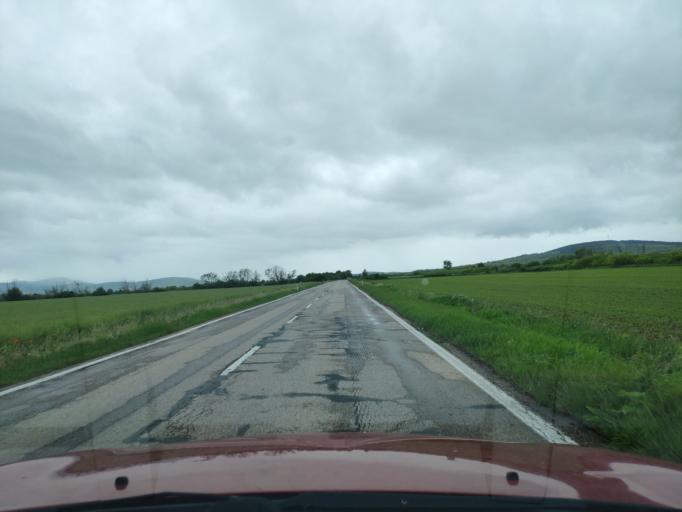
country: HU
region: Borsod-Abauj-Zemplen
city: Satoraljaujhely
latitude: 48.4379
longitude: 21.6560
